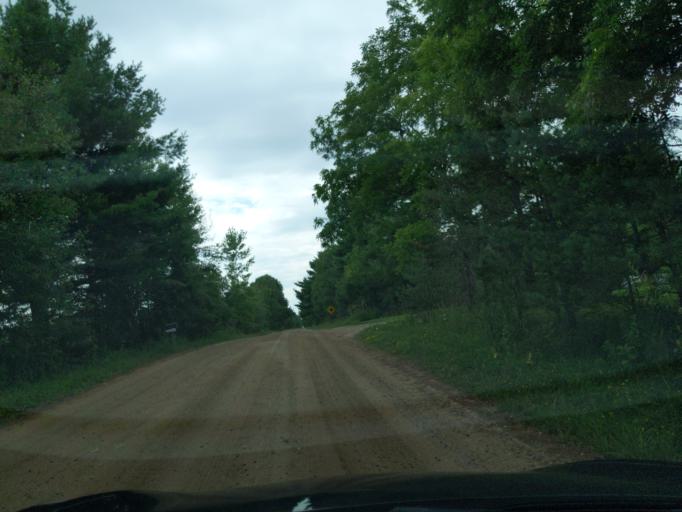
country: US
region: Michigan
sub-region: Clare County
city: Harrison
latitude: 44.0023
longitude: -85.0051
